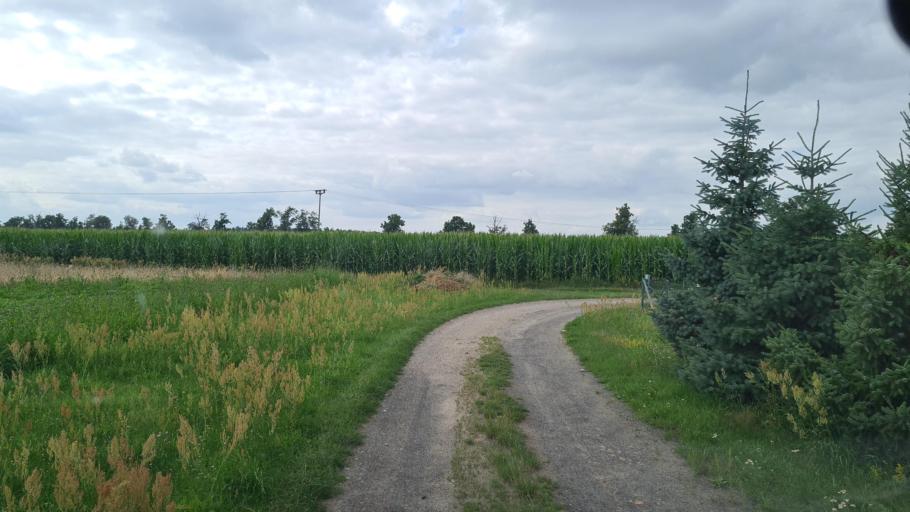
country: DE
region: Brandenburg
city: Altdobern
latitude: 51.6815
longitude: 14.0774
